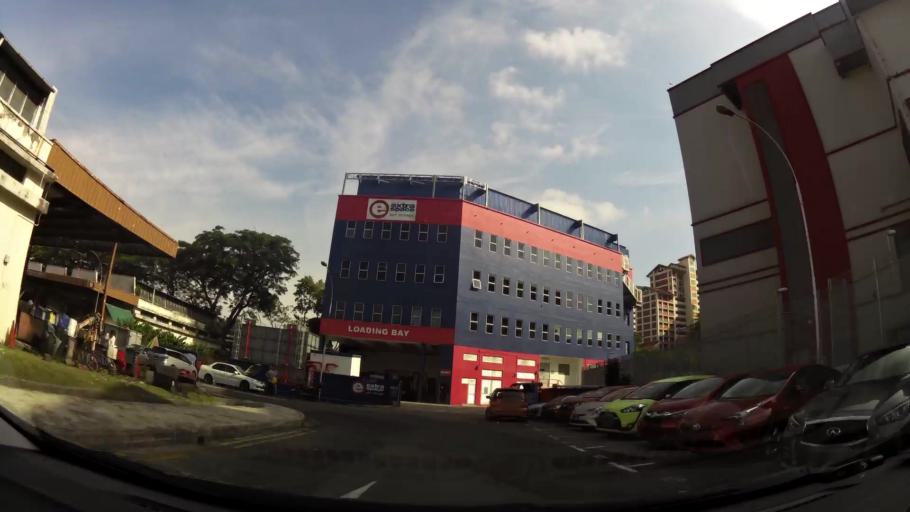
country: SG
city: Singapore
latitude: 1.3569
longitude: 103.8407
